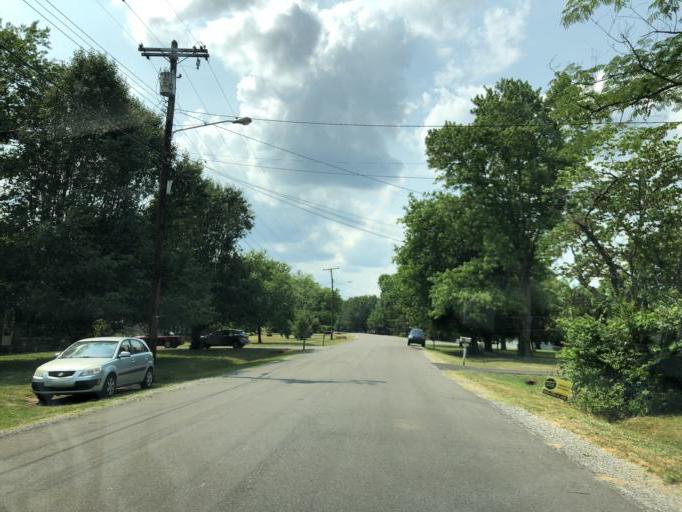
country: US
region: Tennessee
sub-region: Davidson County
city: Goodlettsville
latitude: 36.2535
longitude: -86.7267
